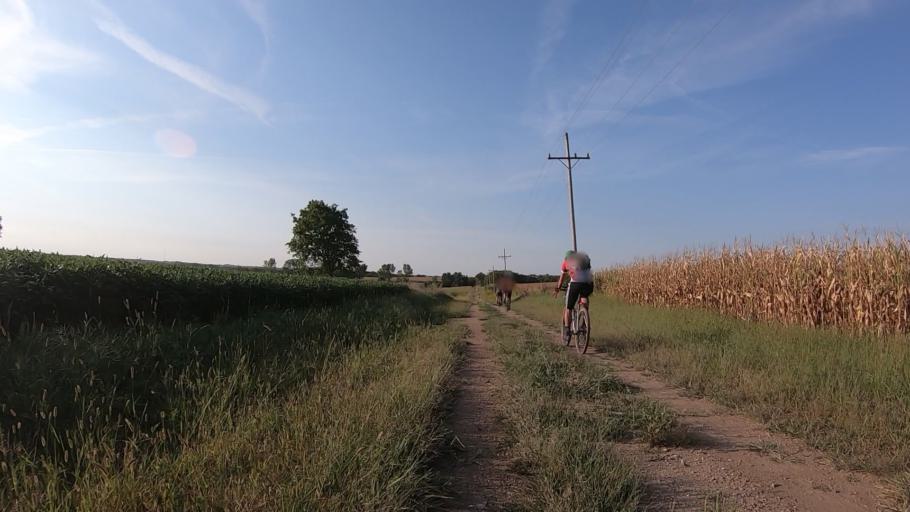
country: US
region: Kansas
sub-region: Marshall County
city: Blue Rapids
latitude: 39.7086
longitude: -96.7792
